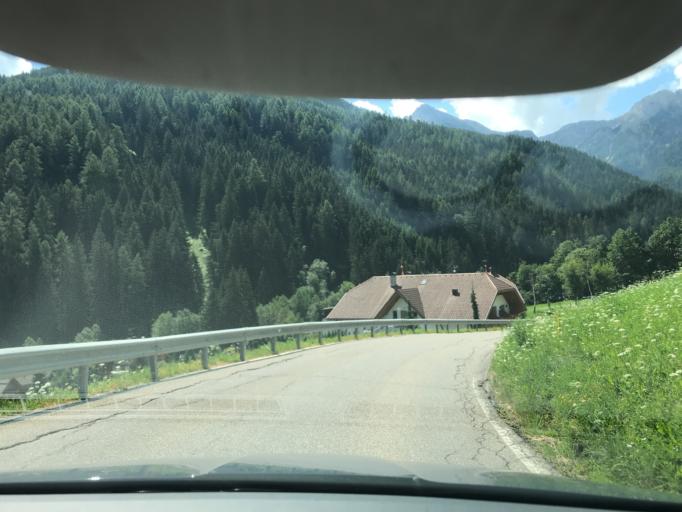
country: IT
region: Trentino-Alto Adige
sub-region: Bolzano
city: Valdaora di Mezzo
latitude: 46.7494
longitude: 12.0111
